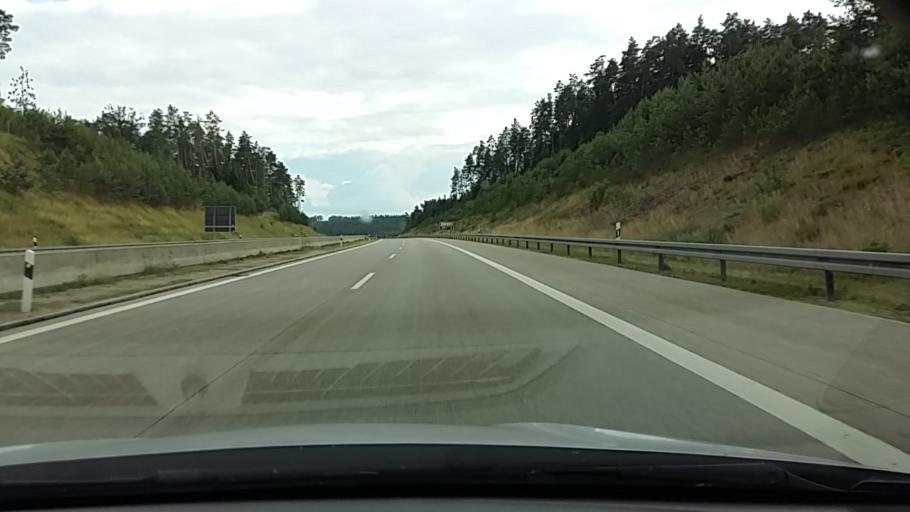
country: DE
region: Bavaria
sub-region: Upper Palatinate
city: Pfreimd
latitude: 49.4896
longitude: 12.1409
